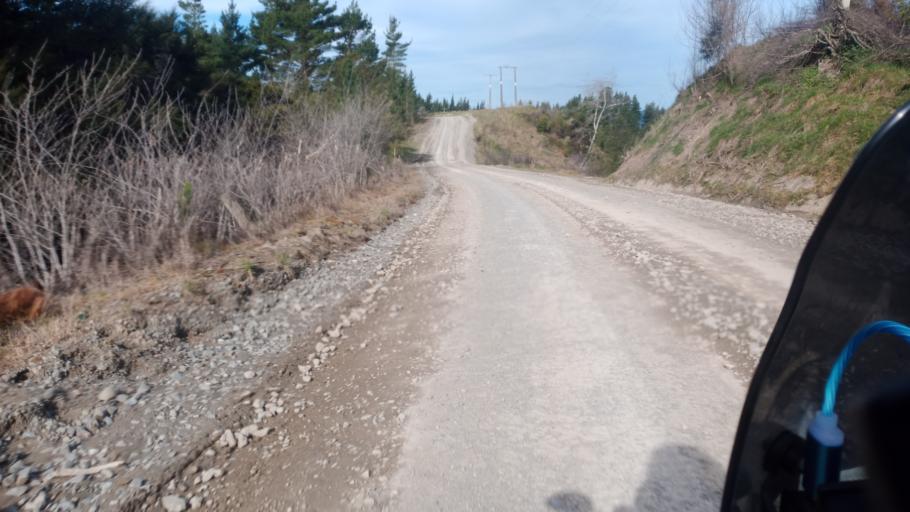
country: NZ
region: Gisborne
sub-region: Gisborne District
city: Gisborne
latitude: -38.1212
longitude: 178.1526
